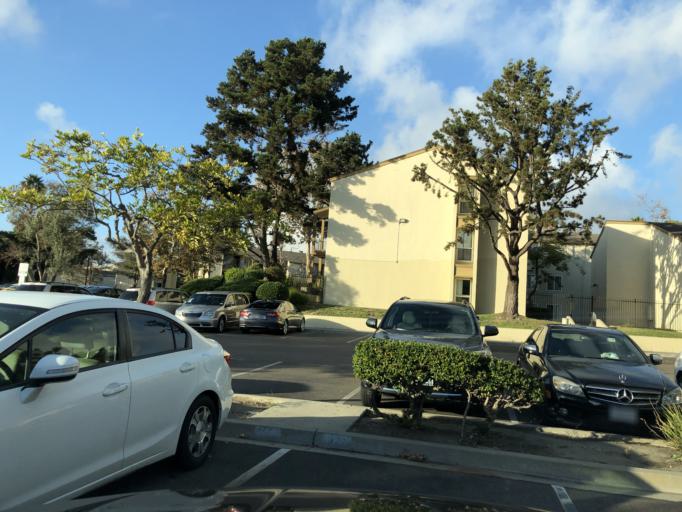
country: US
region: California
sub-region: San Diego County
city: La Jolla
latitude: 32.8161
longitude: -117.1769
